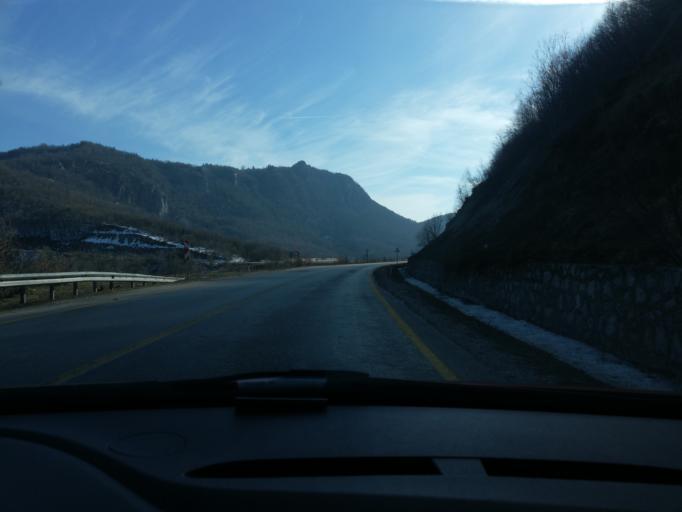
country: TR
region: Kastamonu
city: Cide
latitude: 41.8644
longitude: 33.0532
